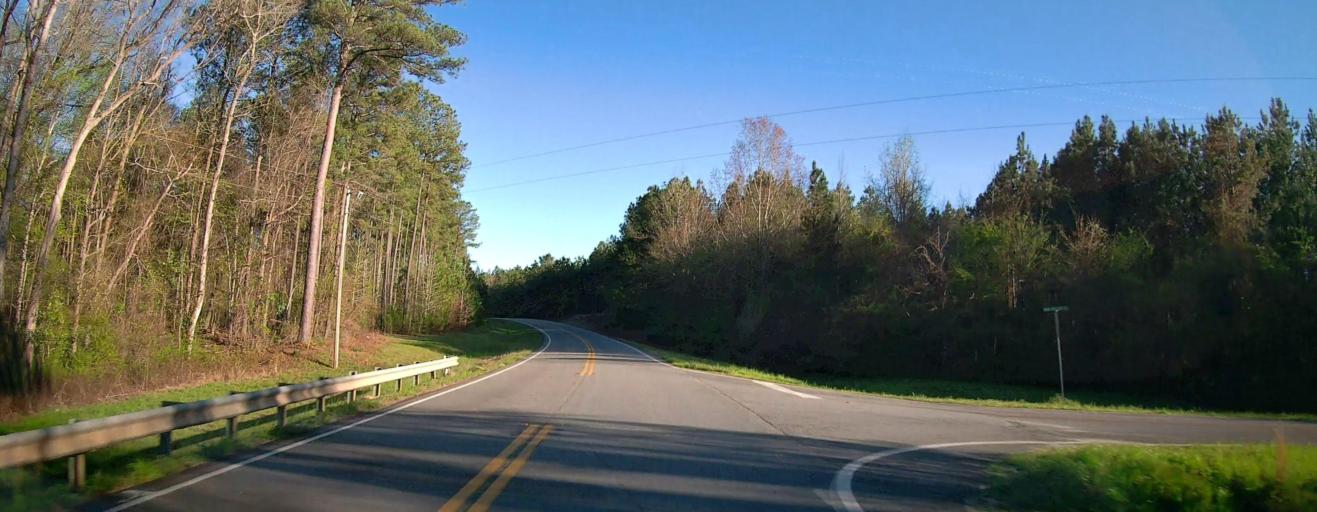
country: US
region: Georgia
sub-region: Wilkinson County
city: Irwinton
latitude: 32.9453
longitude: -83.1626
